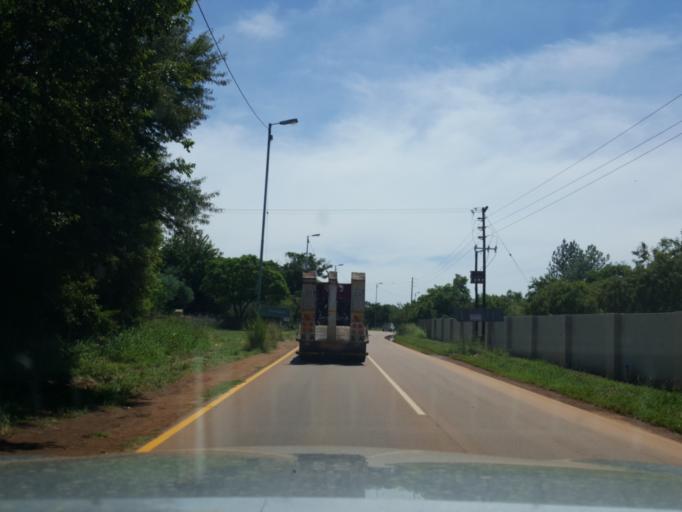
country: ZA
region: Gauteng
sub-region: City of Tshwane Metropolitan Municipality
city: Pretoria
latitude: -25.6695
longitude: 28.3054
